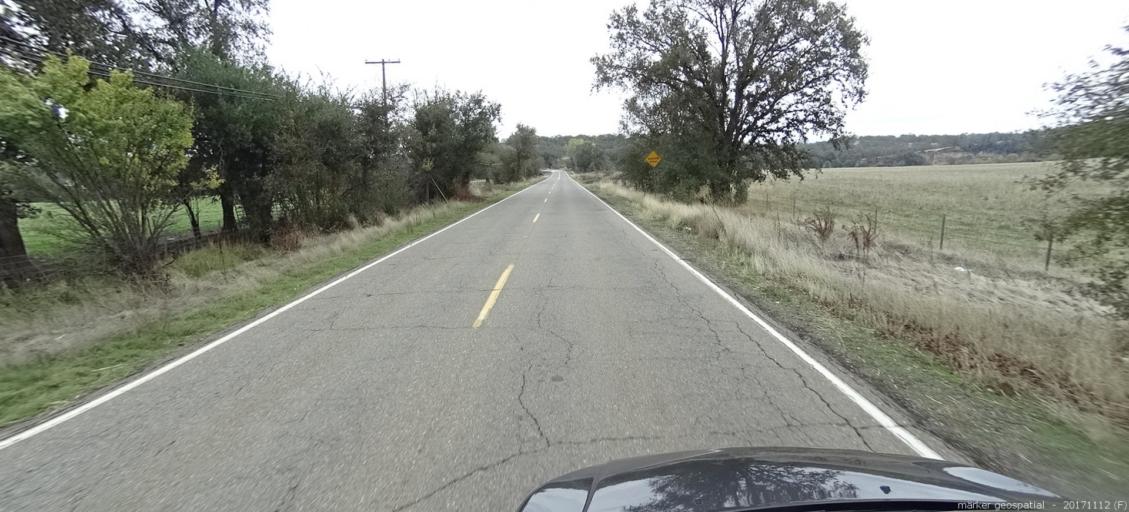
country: US
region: California
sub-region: Shasta County
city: Anderson
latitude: 40.4764
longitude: -122.2330
